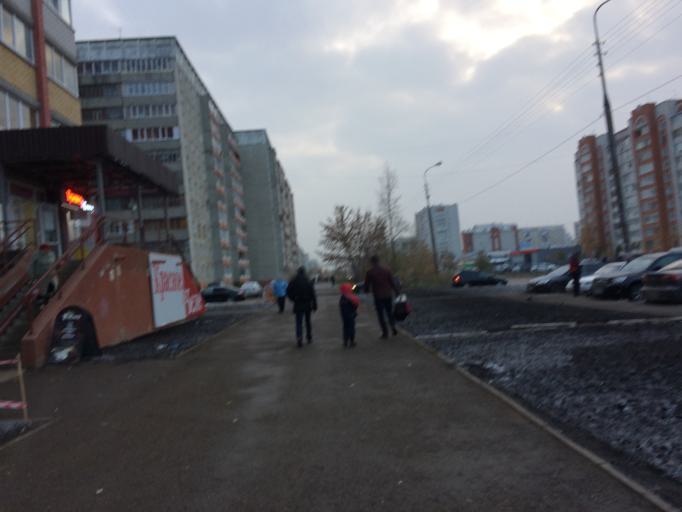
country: RU
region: Mariy-El
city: Yoshkar-Ola
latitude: 56.6385
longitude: 47.9237
